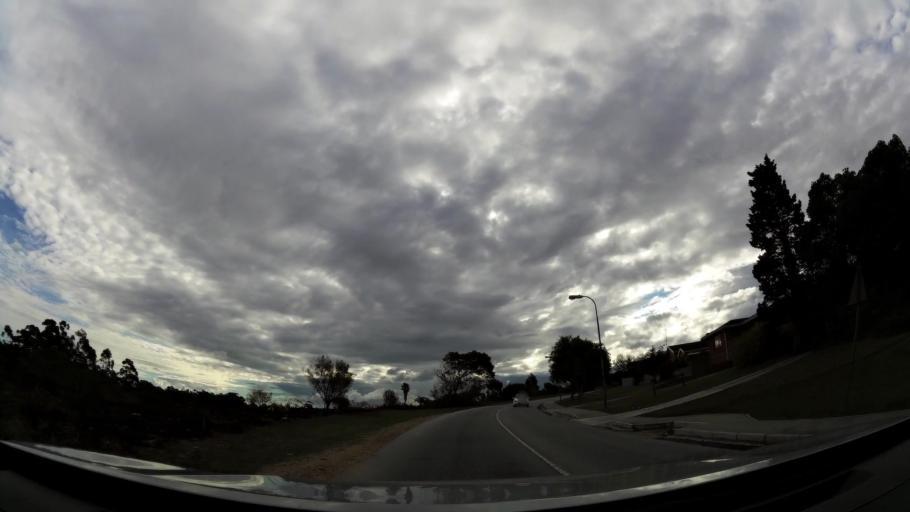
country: ZA
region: Eastern Cape
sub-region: Nelson Mandela Bay Metropolitan Municipality
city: Port Elizabeth
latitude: -33.9525
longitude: 25.5062
